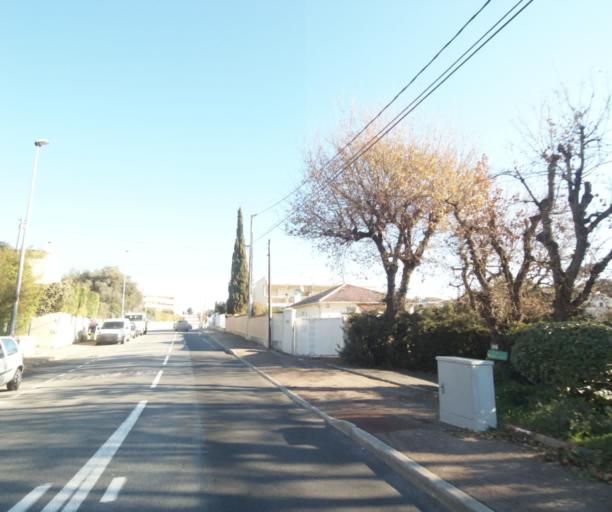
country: FR
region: Provence-Alpes-Cote d'Azur
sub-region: Departement des Alpes-Maritimes
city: Antibes
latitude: 43.5822
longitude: 7.0989
